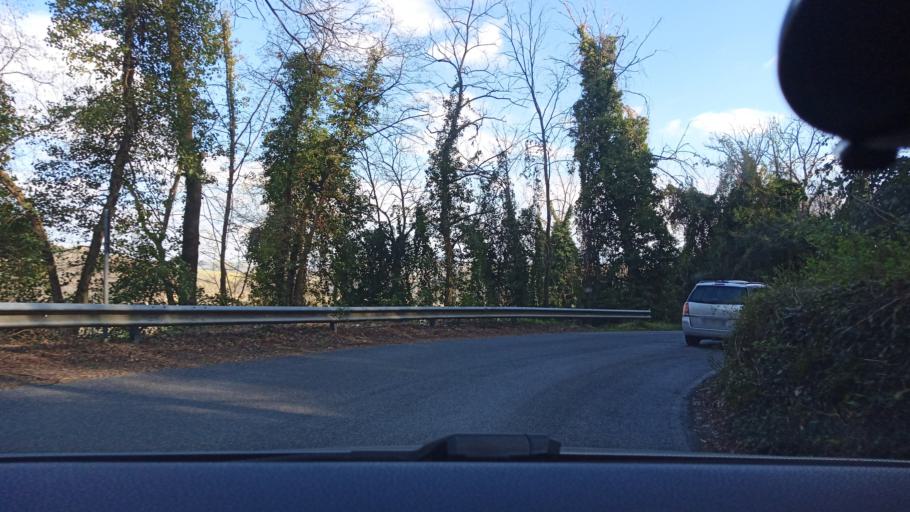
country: IT
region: Latium
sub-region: Citta metropolitana di Roma Capitale
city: Torrita Tiberina
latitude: 42.2418
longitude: 12.6213
